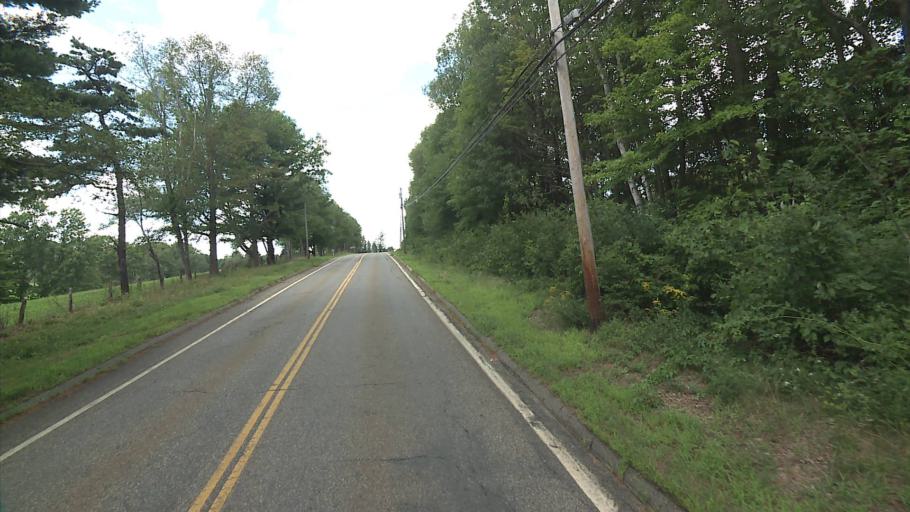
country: US
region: Connecticut
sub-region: Tolland County
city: Stafford
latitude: 41.9436
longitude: -72.1919
